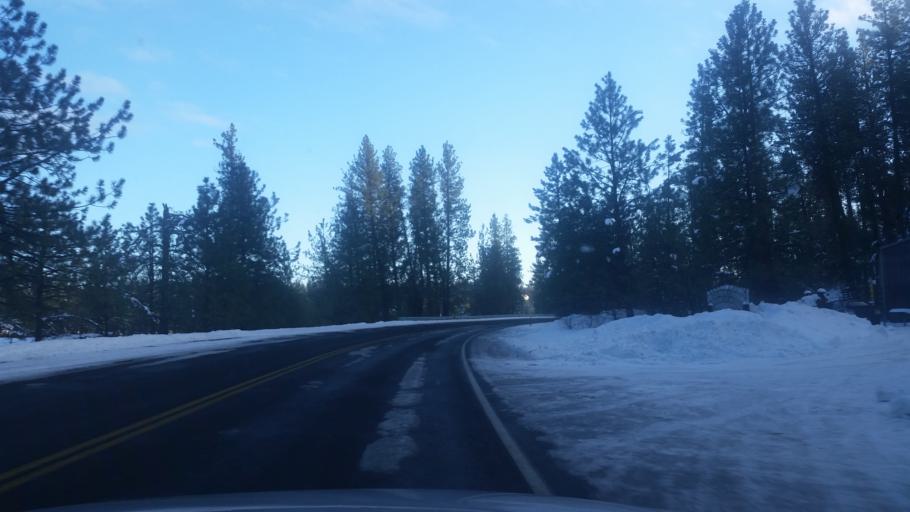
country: US
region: Washington
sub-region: Spokane County
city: Cheney
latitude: 47.5433
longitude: -117.5077
